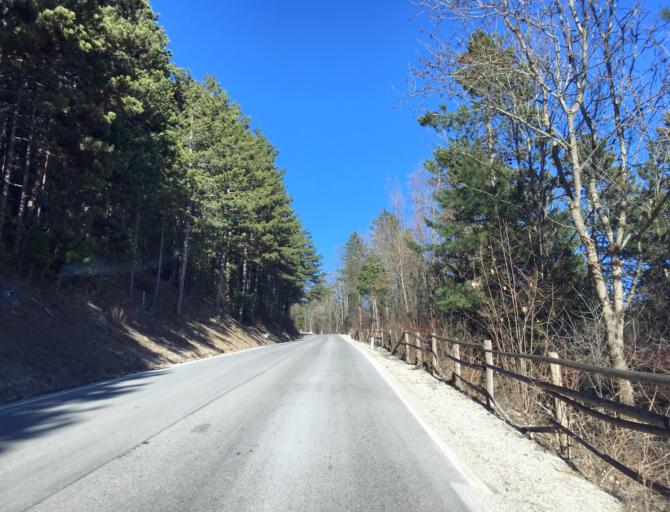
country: AT
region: Lower Austria
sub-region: Politischer Bezirk Wiener Neustadt
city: Waldegg
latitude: 47.8297
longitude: 16.0529
